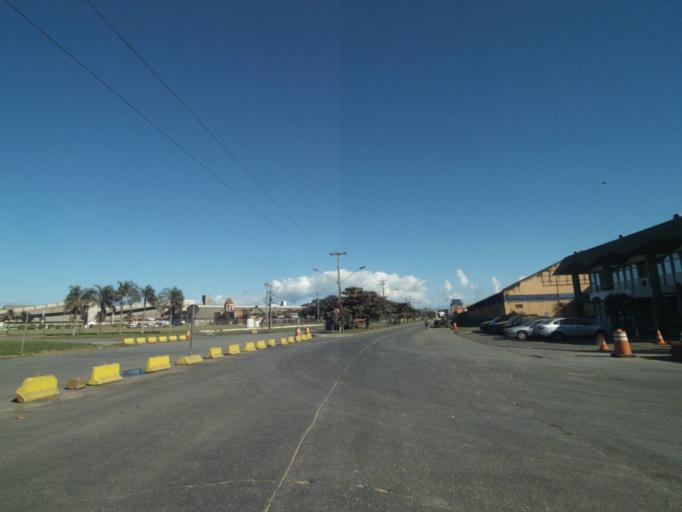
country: BR
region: Parana
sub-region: Paranagua
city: Paranagua
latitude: -25.5040
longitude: -48.5143
